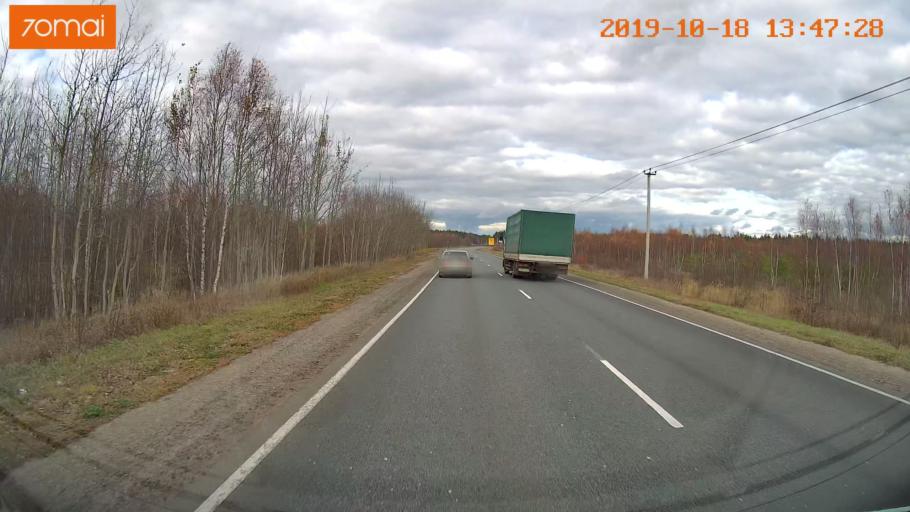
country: RU
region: Moskovskaya
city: Radovitskiy
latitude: 54.9756
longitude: 39.9514
